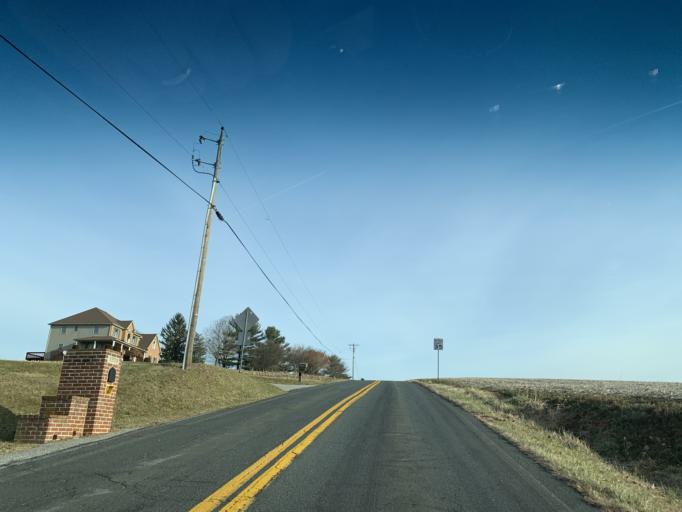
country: US
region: Maryland
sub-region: Carroll County
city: Hampstead
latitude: 39.5990
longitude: -76.8820
